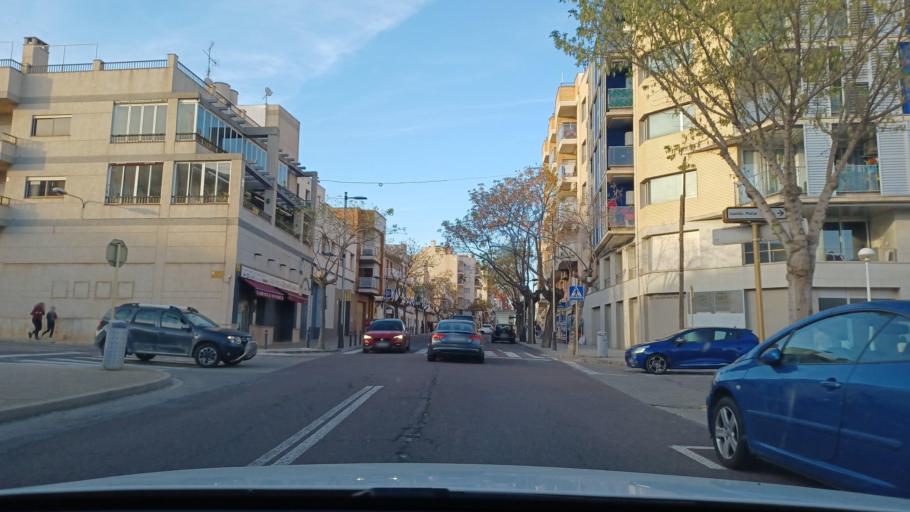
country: ES
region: Catalonia
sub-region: Provincia de Tarragona
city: Sant Carles de la Rapita
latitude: 40.6131
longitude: 0.5863
